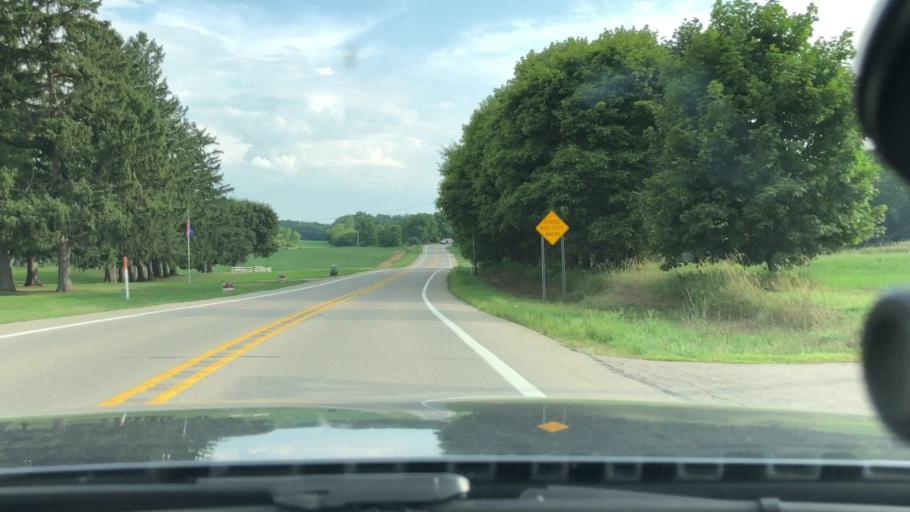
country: US
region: Michigan
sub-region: Washtenaw County
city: Manchester
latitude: 42.1699
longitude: -84.0317
